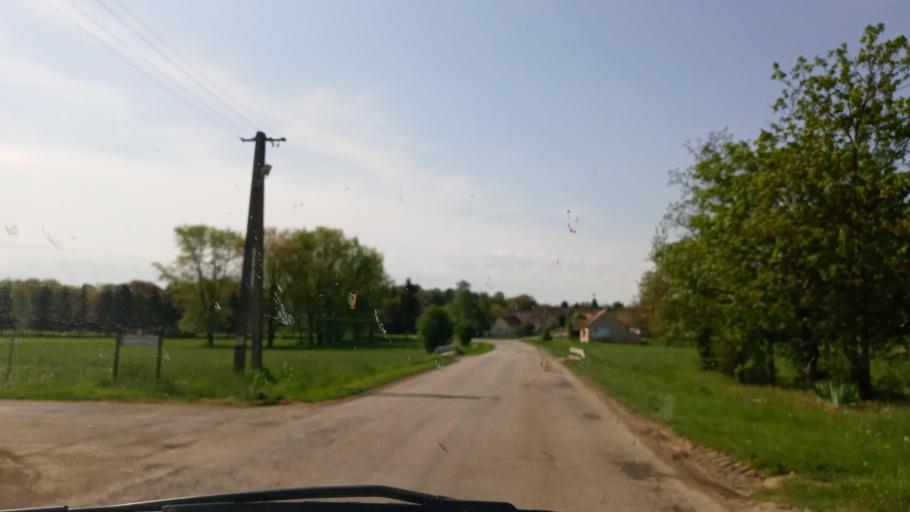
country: HU
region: Baranya
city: Boly
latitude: 45.9484
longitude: 18.5728
